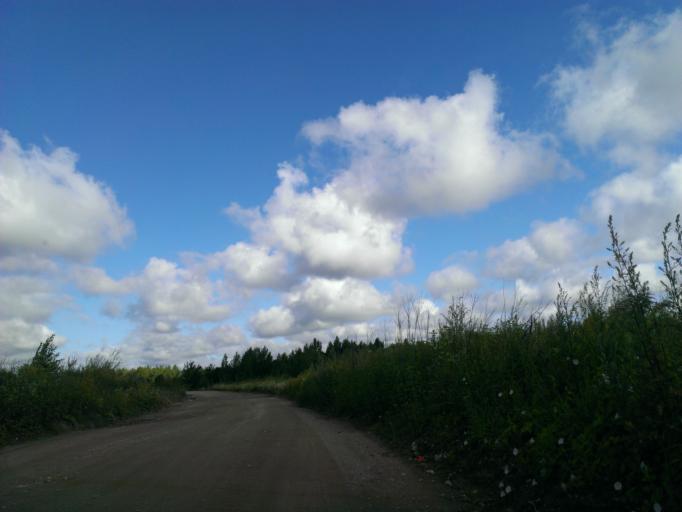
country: LV
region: Incukalns
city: Vangazi
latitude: 57.0901
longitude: 24.5132
